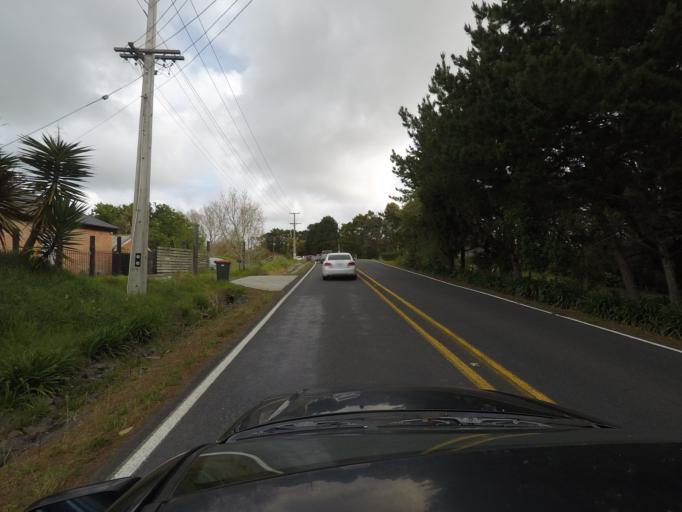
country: NZ
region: Auckland
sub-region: Auckland
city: Pakuranga
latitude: -36.9401
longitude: 174.9459
